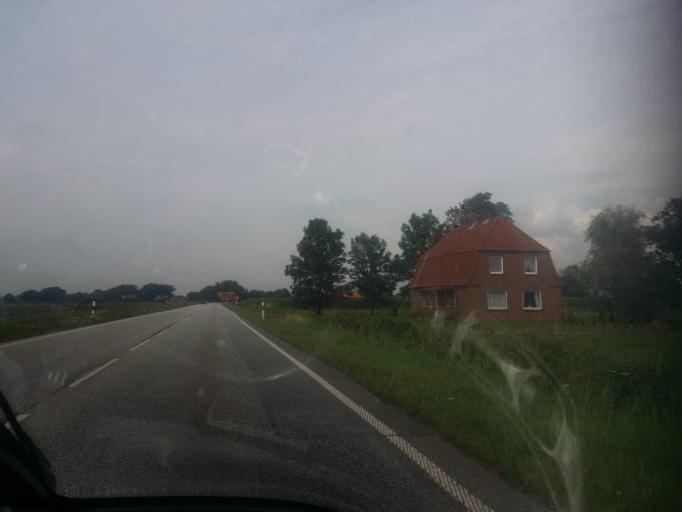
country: DE
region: Schleswig-Holstein
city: Meldorf
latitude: 54.0998
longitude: 9.0598
